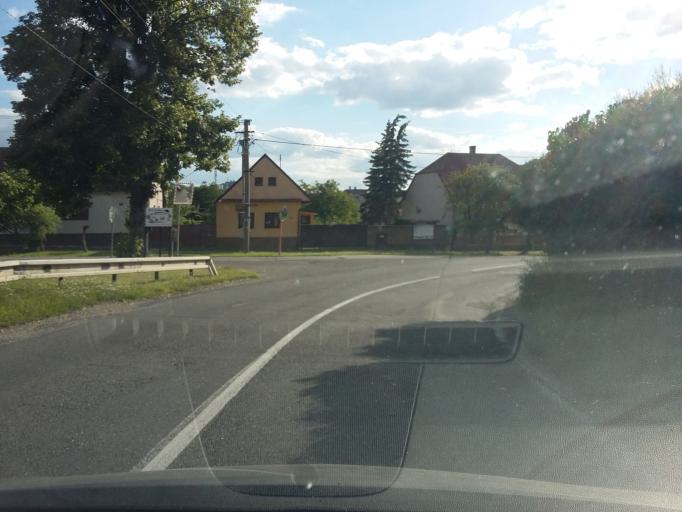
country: SK
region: Trnavsky
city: Smolenice
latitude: 48.5127
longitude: 17.3025
